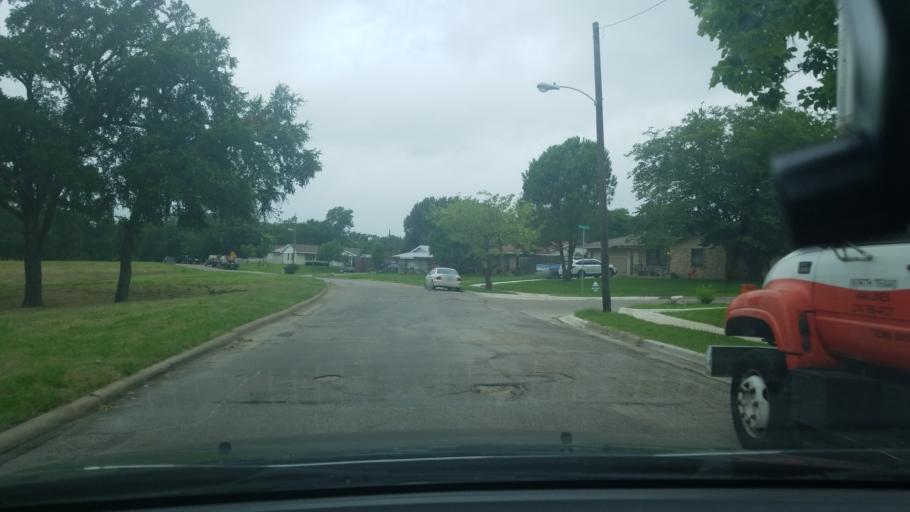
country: US
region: Texas
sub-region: Dallas County
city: Mesquite
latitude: 32.7883
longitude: -96.6365
